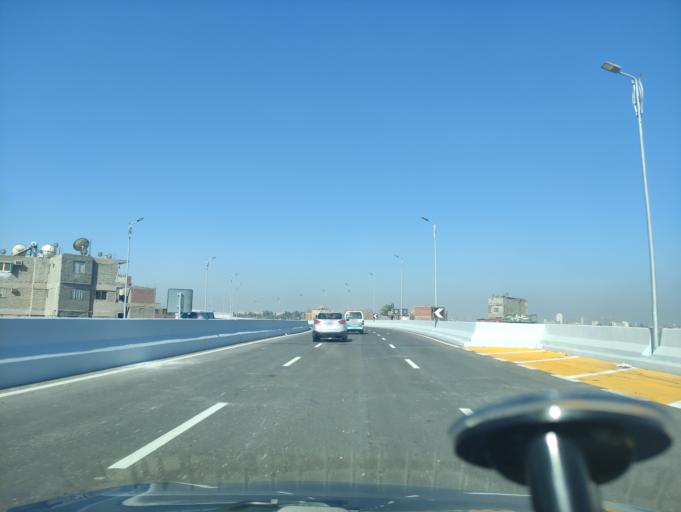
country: EG
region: Al Jizah
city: Al Jizah
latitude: 30.0081
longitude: 31.2594
